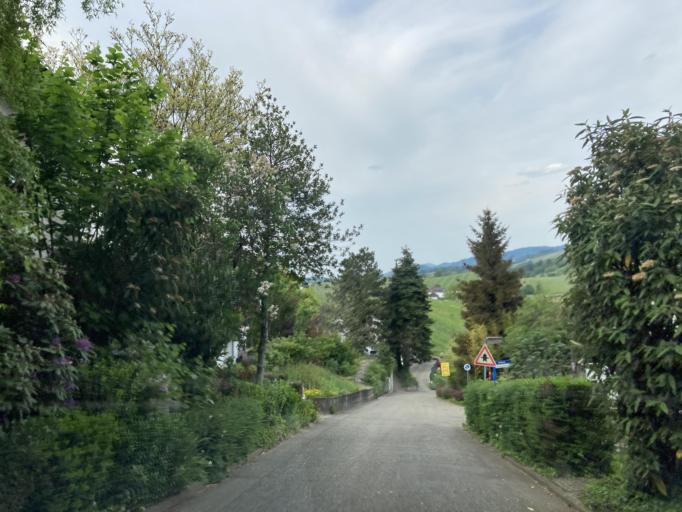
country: DE
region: Baden-Wuerttemberg
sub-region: Freiburg Region
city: Sasbachwalden
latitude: 48.6163
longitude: 8.1106
